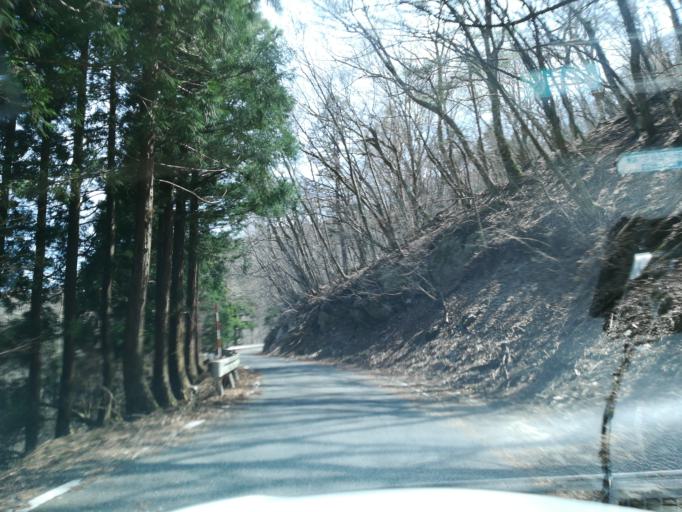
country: JP
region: Tokushima
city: Wakimachi
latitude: 33.8832
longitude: 134.0516
